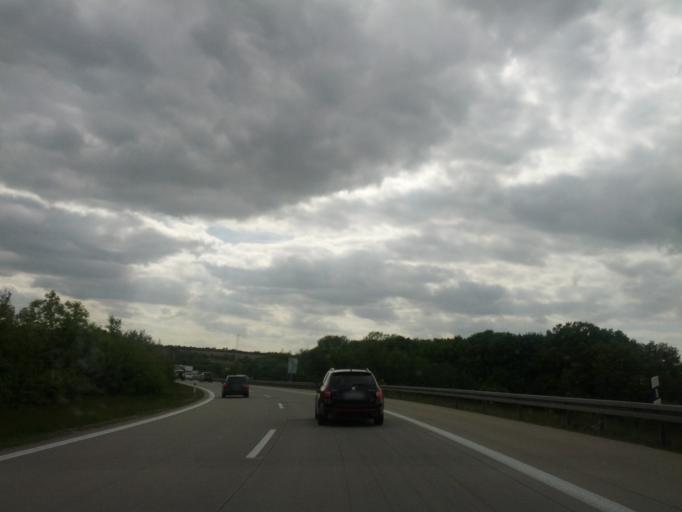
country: DE
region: Saxony
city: Wilsdruff
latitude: 51.0639
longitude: 13.6023
